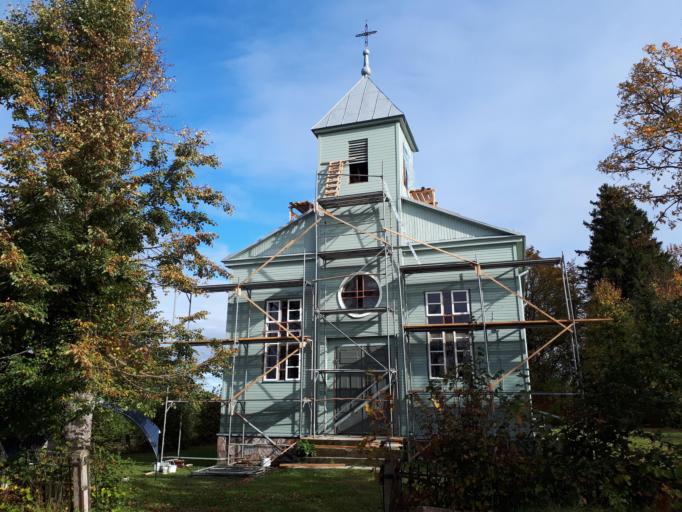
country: LT
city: Ignalina
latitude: 55.4419
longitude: 25.9493
